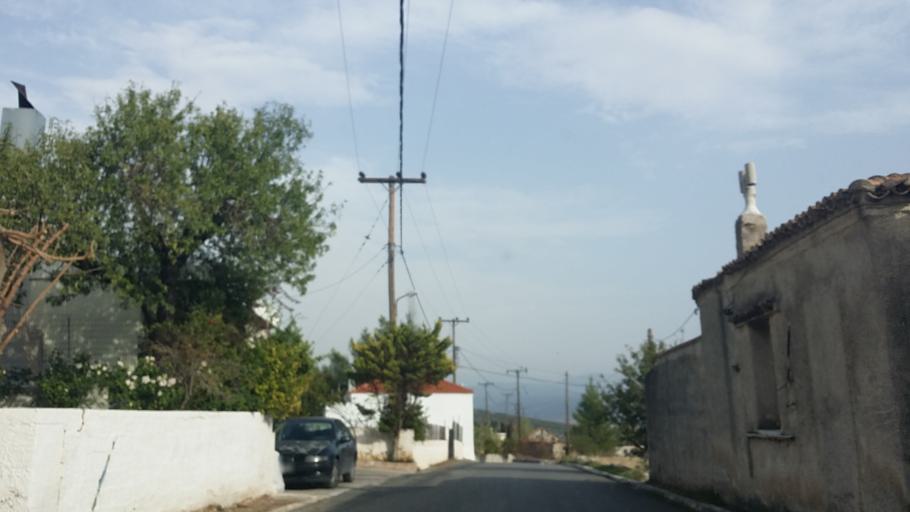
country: GR
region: Central Greece
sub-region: Nomos Voiotias
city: Korini
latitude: 38.2584
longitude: 22.9119
